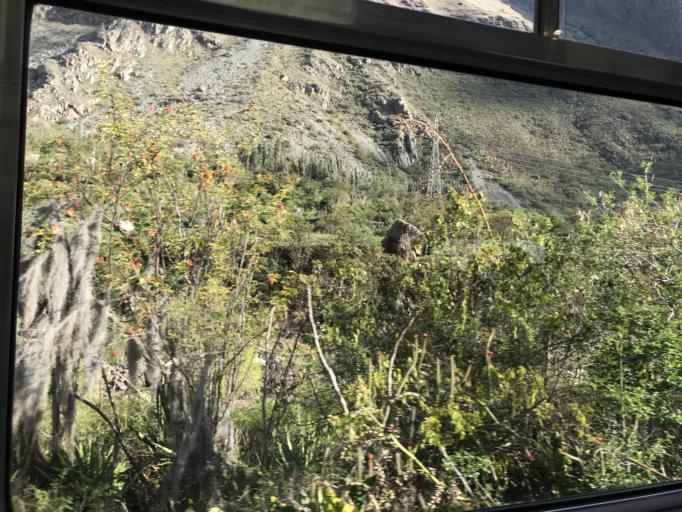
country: PE
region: Cusco
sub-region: Provincia de Urubamba
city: Ollantaytambo
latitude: -13.2276
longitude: -72.4043
